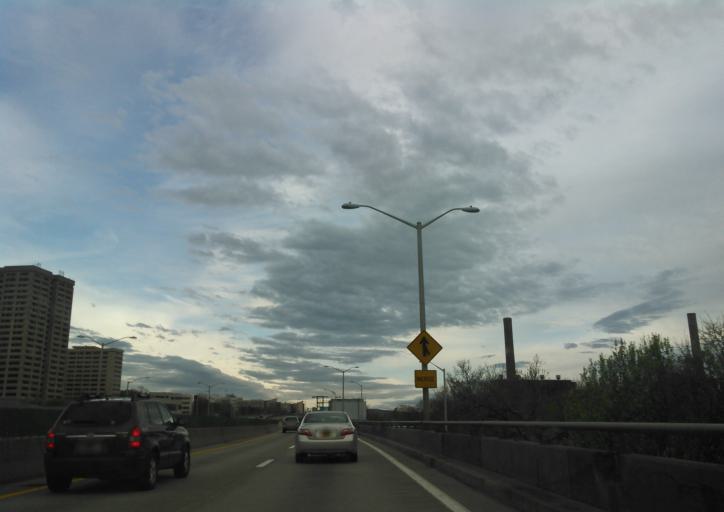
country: US
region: New York
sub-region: Onondaga County
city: Syracuse
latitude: 43.0416
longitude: -76.1426
